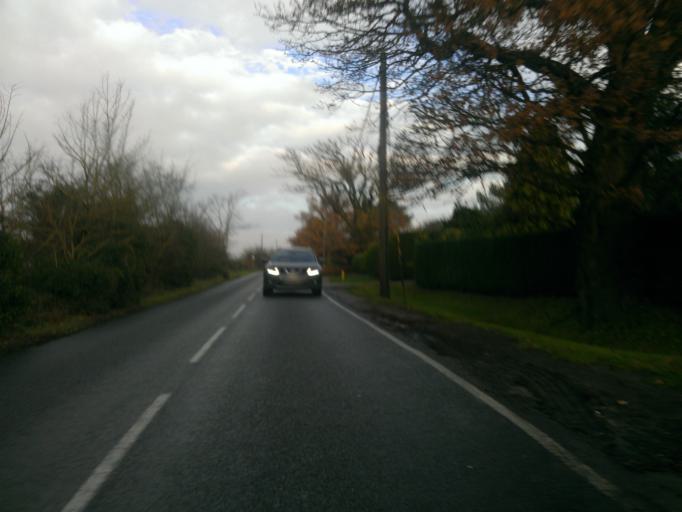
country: GB
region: England
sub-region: Essex
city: Wivenhoe
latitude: 51.8553
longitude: 0.9774
